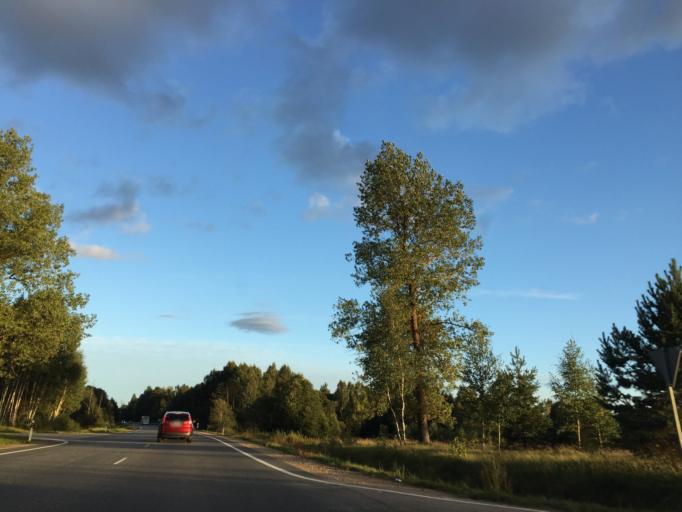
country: LV
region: Broceni
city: Broceni
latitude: 56.6704
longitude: 22.5892
